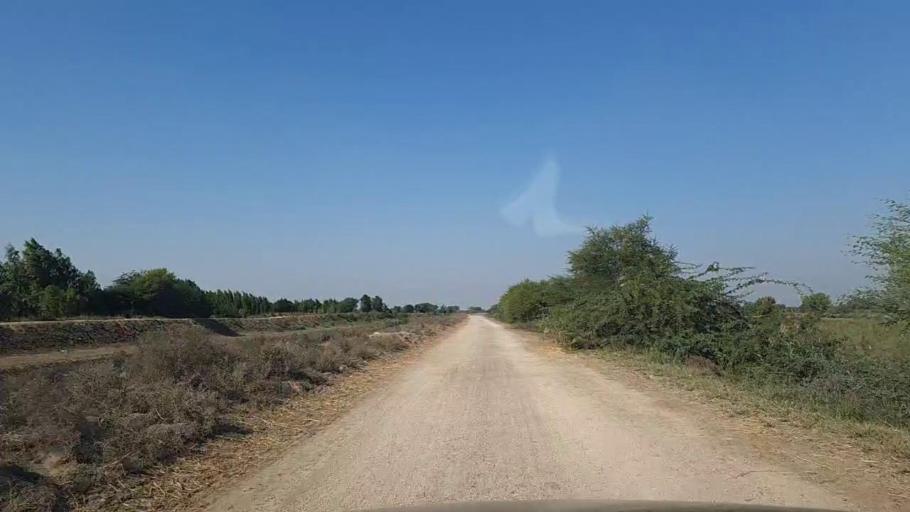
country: PK
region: Sindh
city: Mirpur Batoro
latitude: 24.7282
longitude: 68.2300
